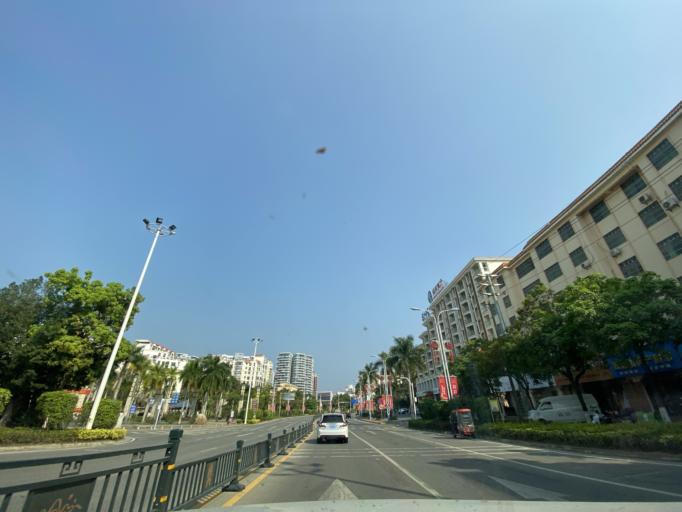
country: CN
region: Hainan
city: Chongshan
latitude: 18.7660
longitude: 109.5207
